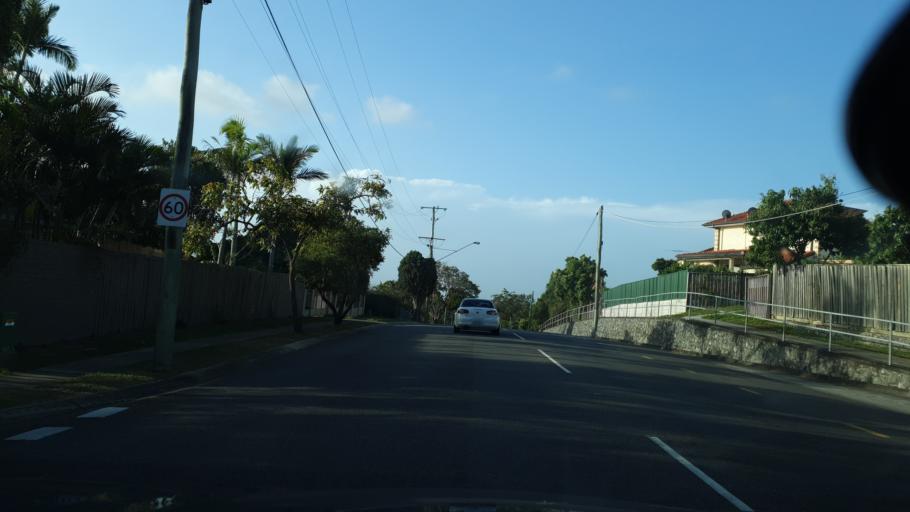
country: AU
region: Queensland
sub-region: Brisbane
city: Belmont
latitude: -27.4889
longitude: 153.1273
